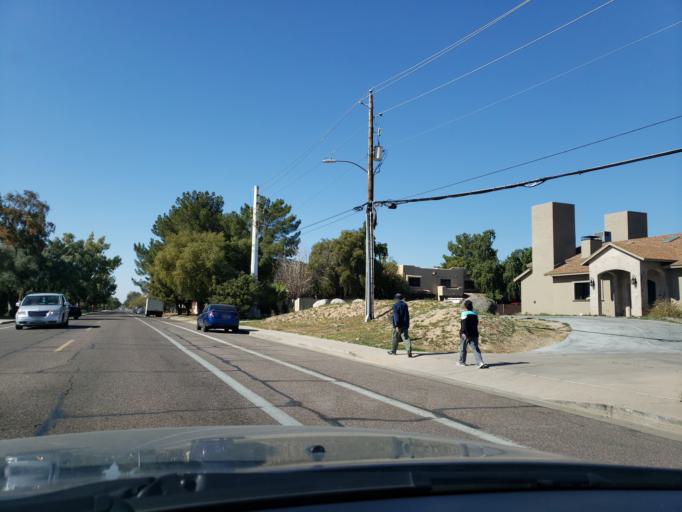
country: US
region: Arizona
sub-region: Maricopa County
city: Paradise Valley
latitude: 33.6476
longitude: -112.0499
